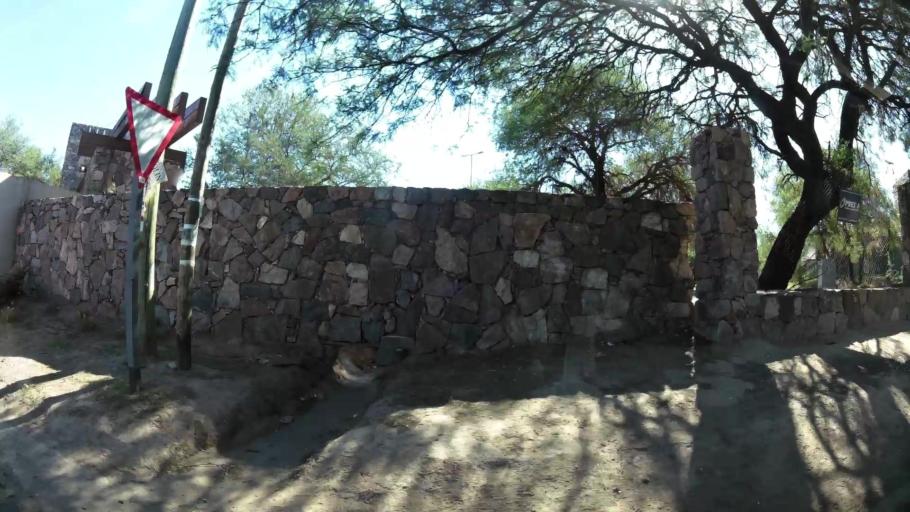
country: AR
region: Cordoba
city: La Calera
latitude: -31.3501
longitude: -64.3101
